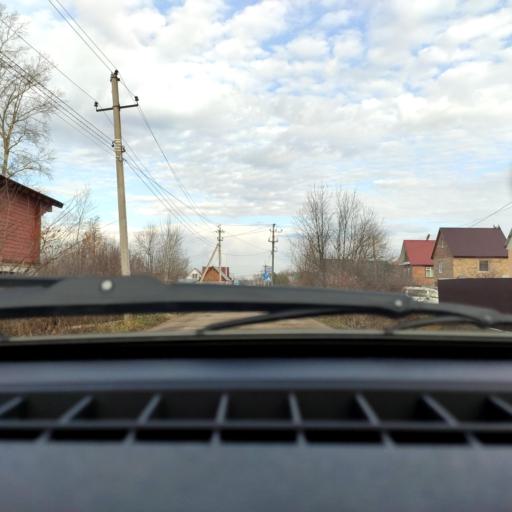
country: RU
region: Bashkortostan
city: Ufa
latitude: 54.6305
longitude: 55.8901
